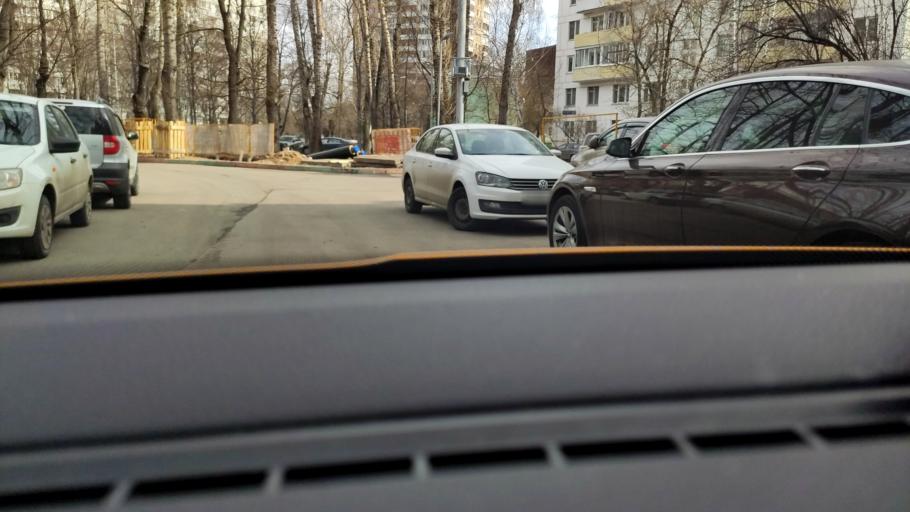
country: RU
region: Moscow
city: Sokol'niki
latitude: 55.8087
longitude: 37.6501
